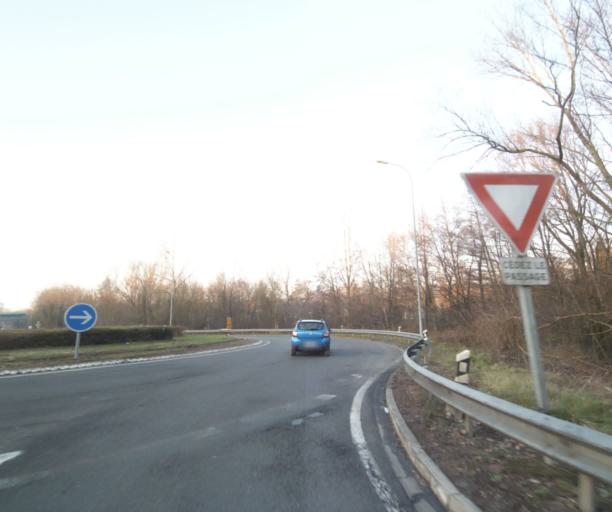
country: FR
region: Lorraine
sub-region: Departement de la Meuse
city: Ancerville
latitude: 48.6225
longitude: 4.9938
